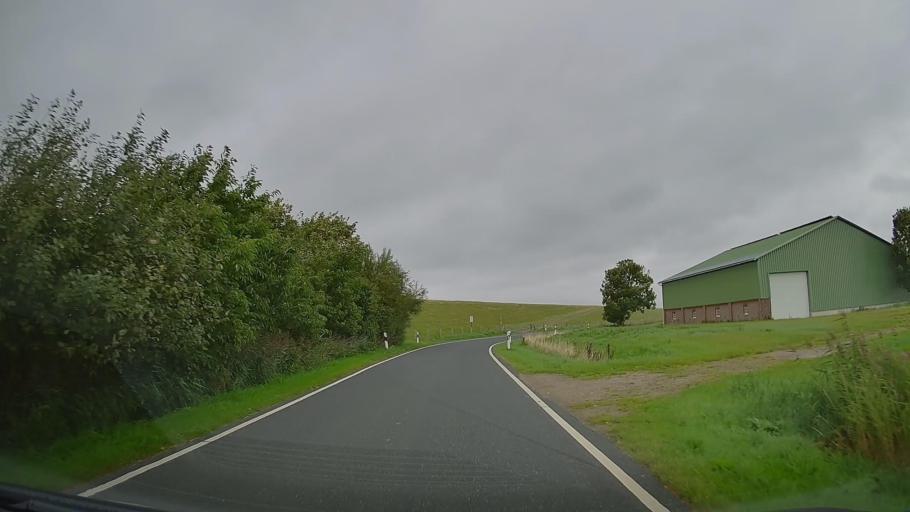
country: DE
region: Schleswig-Holstein
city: Friedrichskoog
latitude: 54.0266
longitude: 8.9196
